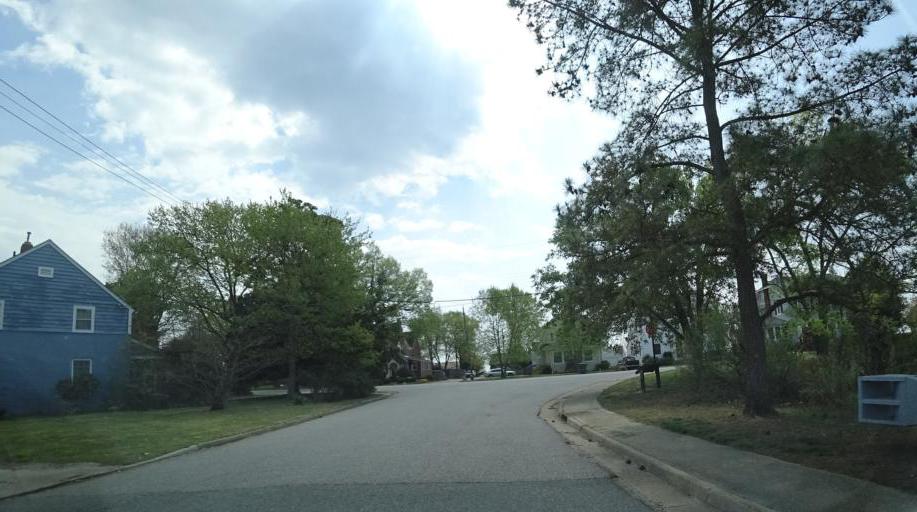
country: US
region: Virginia
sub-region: City of Hampton
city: Hampton
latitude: 37.0000
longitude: -76.3735
